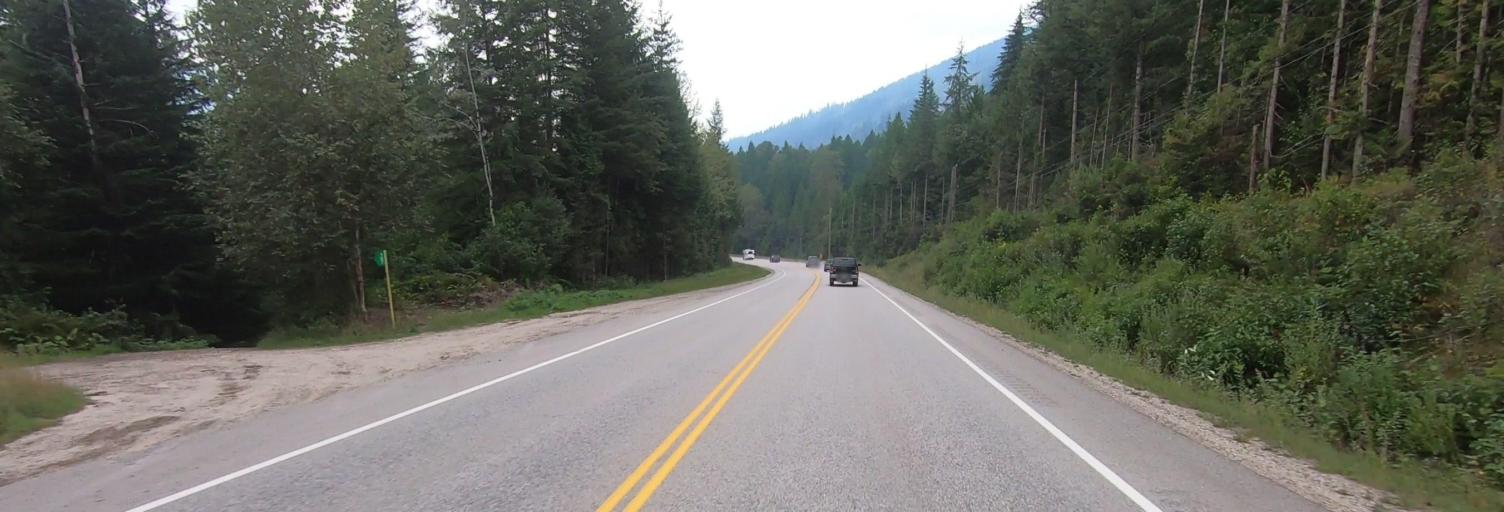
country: CA
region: British Columbia
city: Revelstoke
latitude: 50.9769
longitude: -118.5273
